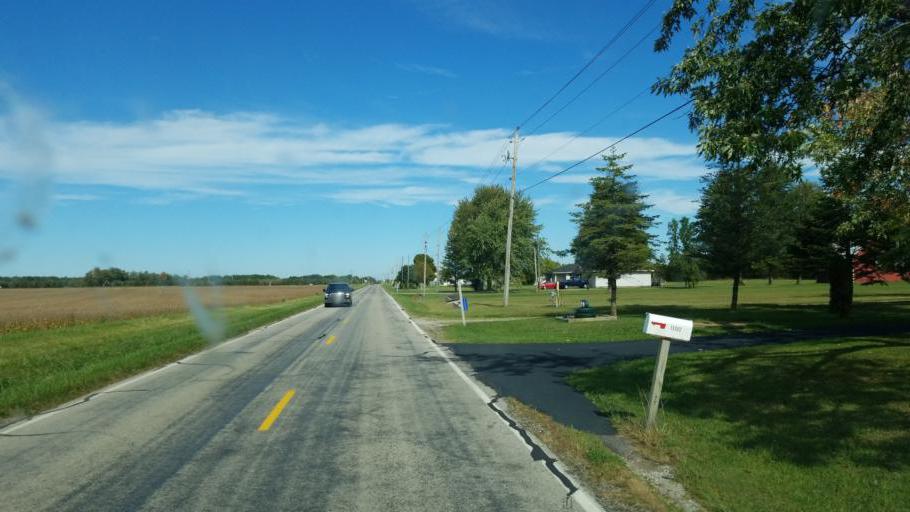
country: US
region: Ohio
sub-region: Huron County
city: Wakeman
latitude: 41.2977
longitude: -82.4926
